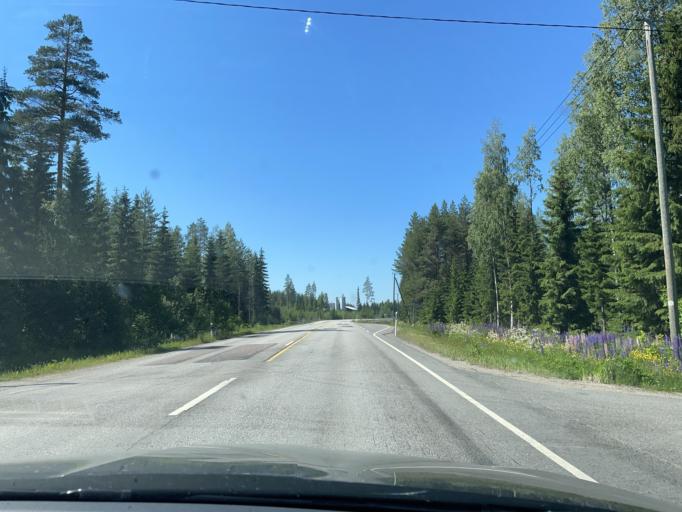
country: FI
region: Central Finland
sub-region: Saarijaervi-Viitasaari
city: Viitasaari
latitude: 63.1404
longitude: 25.7843
